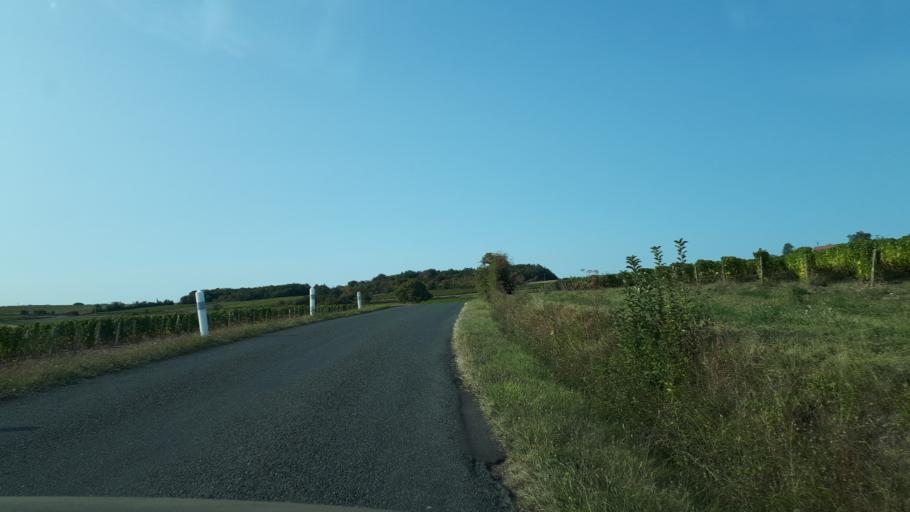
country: FR
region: Centre
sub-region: Departement du Cher
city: Menetou-Salon
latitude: 47.2275
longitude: 2.5196
